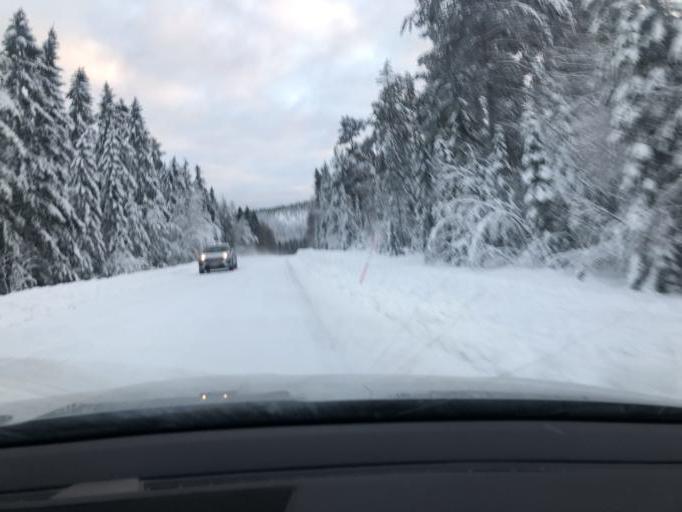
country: SE
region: Vaesternorrland
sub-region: Kramfors Kommun
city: Nordingra
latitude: 62.9908
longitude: 18.2544
